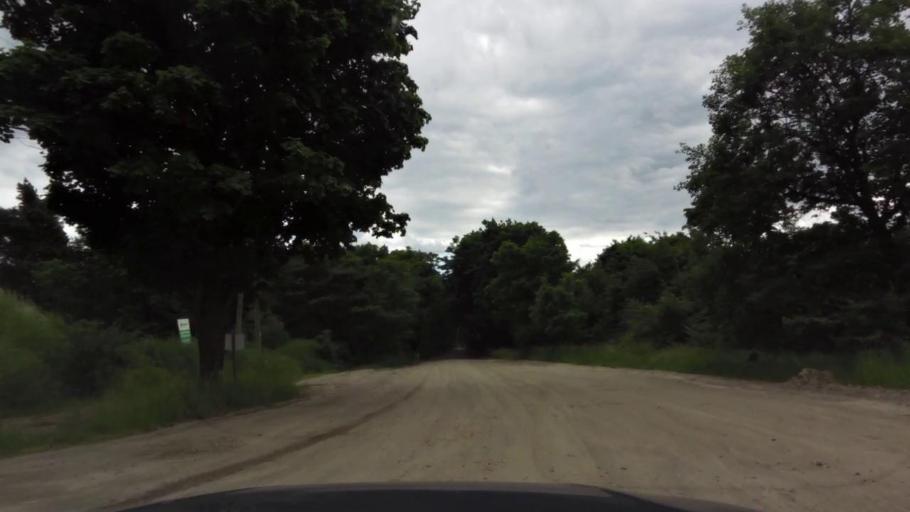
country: PL
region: West Pomeranian Voivodeship
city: Trzcinsko Zdroj
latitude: 52.8715
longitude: 14.5844
